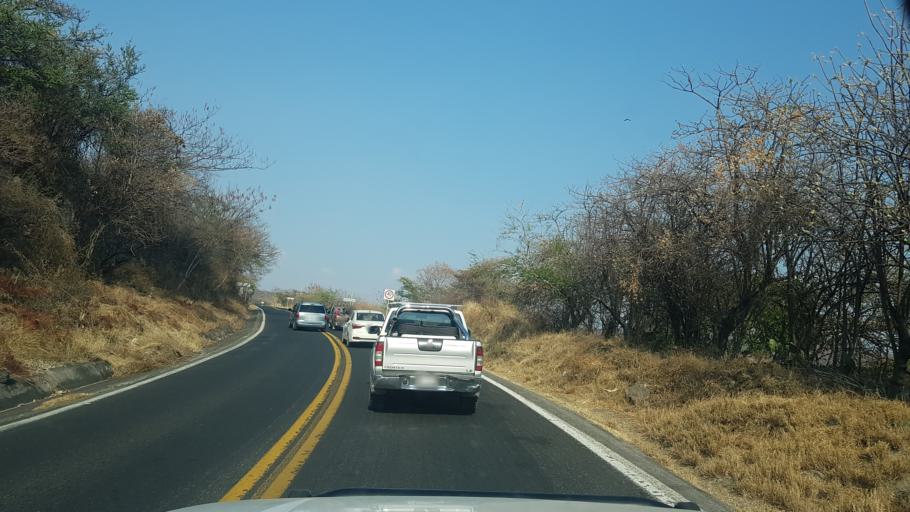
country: MX
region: Puebla
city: Calmeca
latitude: 18.6425
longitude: -98.6381
